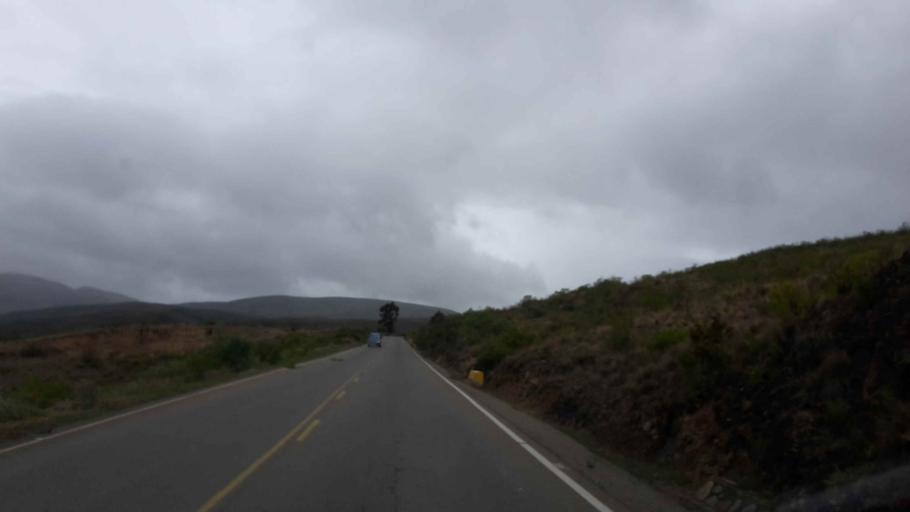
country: BO
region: Cochabamba
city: Arani
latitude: -17.4723
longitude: -65.7642
